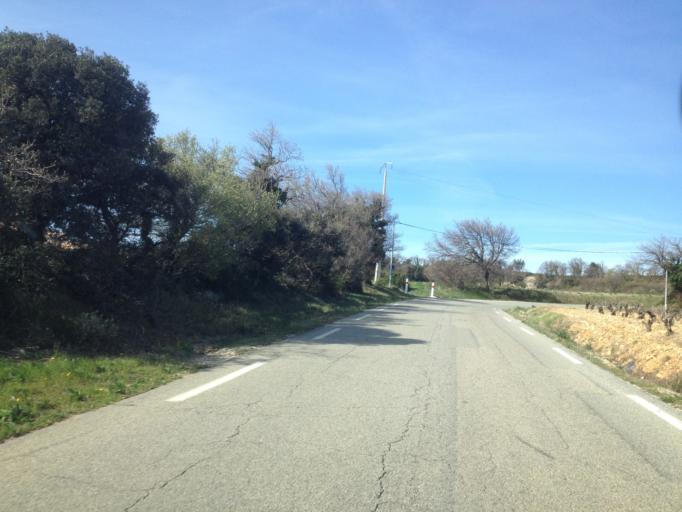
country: FR
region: Provence-Alpes-Cote d'Azur
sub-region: Departement du Vaucluse
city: Bedarrides
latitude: 44.0473
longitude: 4.8817
